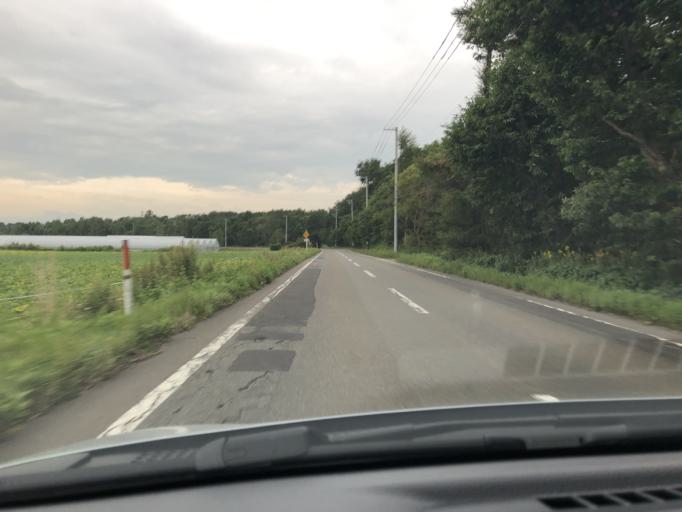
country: JP
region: Hokkaido
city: Chitose
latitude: 42.8719
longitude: 141.7231
